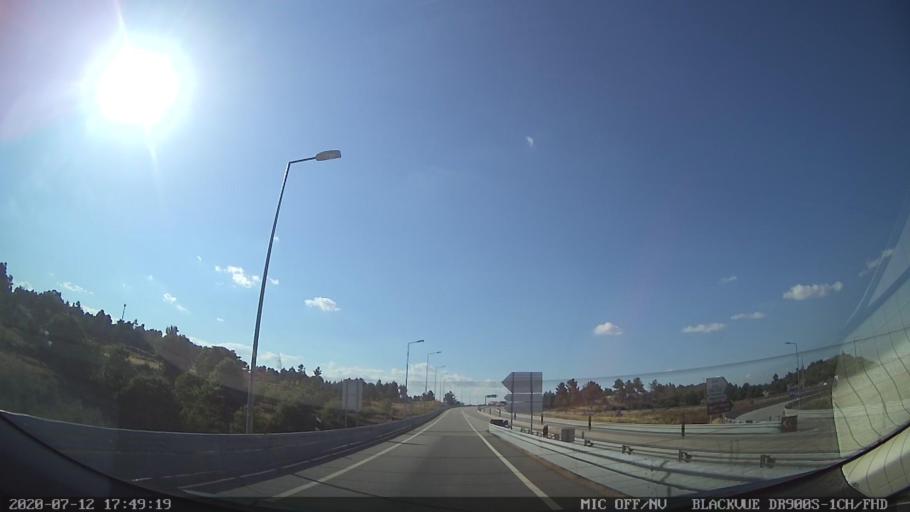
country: PT
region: Vila Real
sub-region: Murca
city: Murca
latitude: 41.3433
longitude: -7.4698
